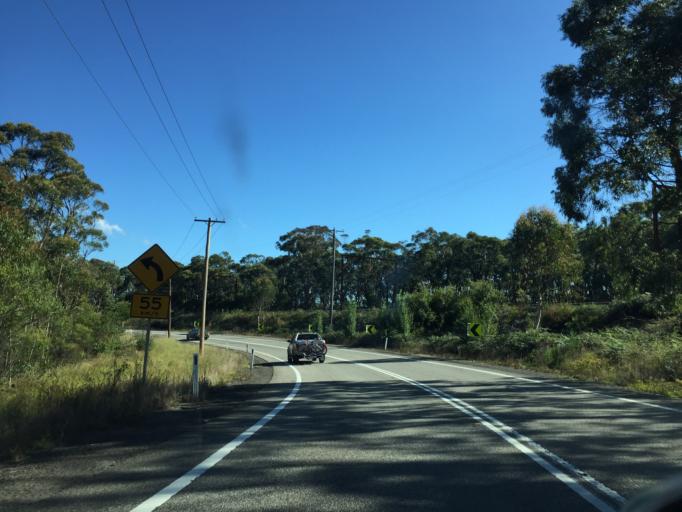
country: AU
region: New South Wales
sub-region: Blue Mountains Municipality
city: Blackheath
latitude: -33.6622
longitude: 150.2780
